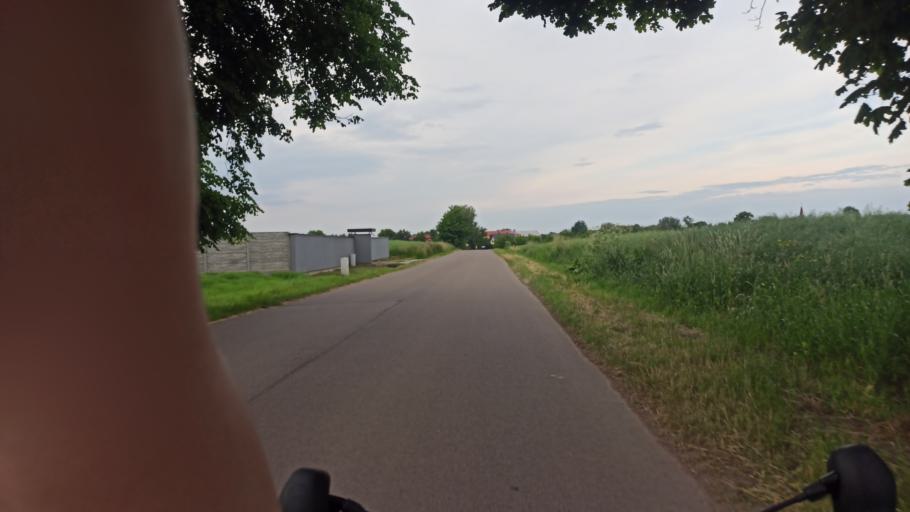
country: PL
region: Subcarpathian Voivodeship
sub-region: Powiat jaroslawski
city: Radymno
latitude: 49.9288
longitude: 22.8064
